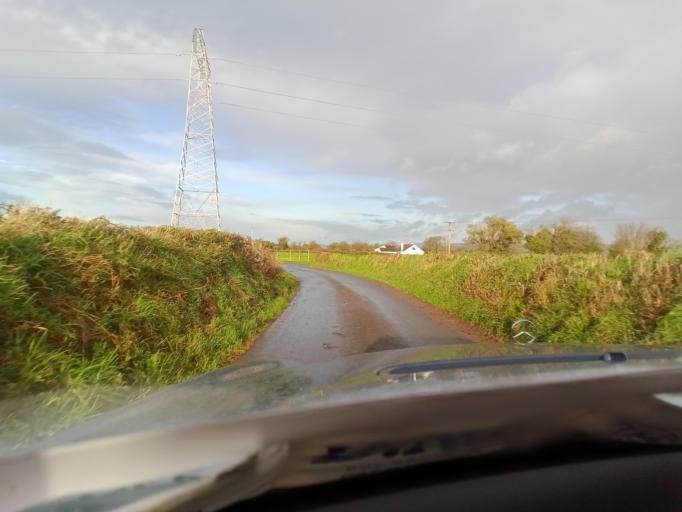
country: IE
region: Leinster
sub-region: Kilkenny
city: Mooncoin
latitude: 52.2780
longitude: -7.1932
